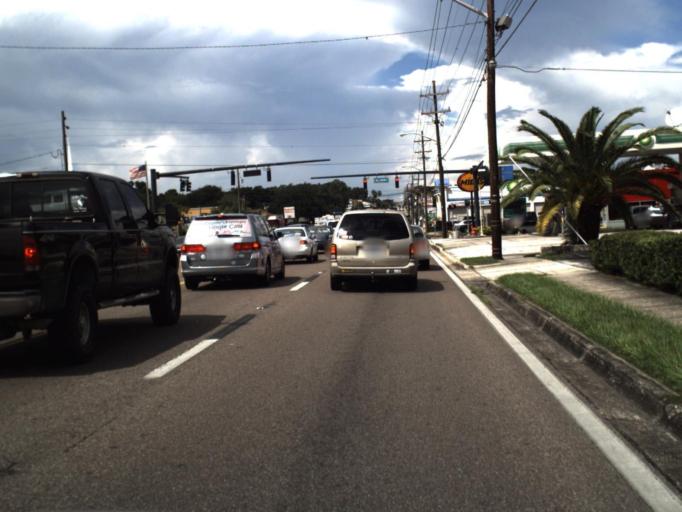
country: US
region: Florida
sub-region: Polk County
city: Lakeland
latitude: 28.0027
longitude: -81.9569
